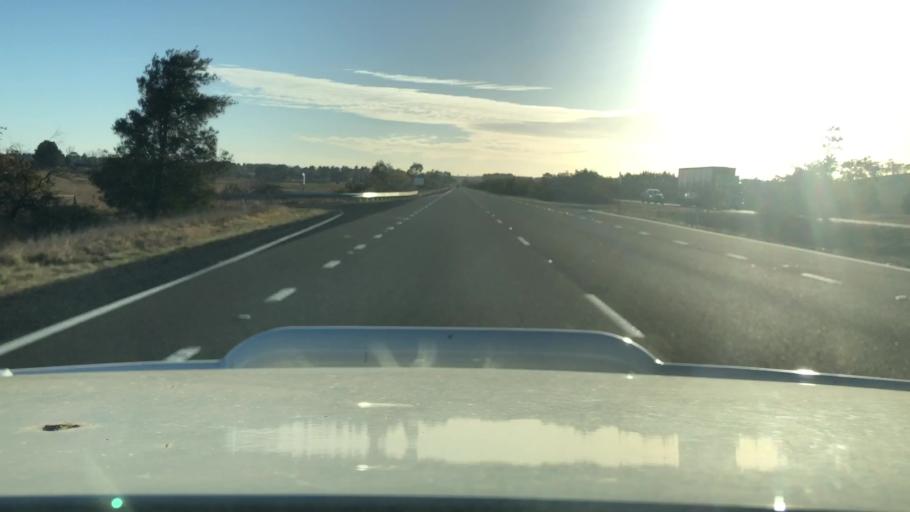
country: AU
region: New South Wales
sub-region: Wingecarribee
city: Moss Vale
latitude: -34.5446
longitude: 150.2734
